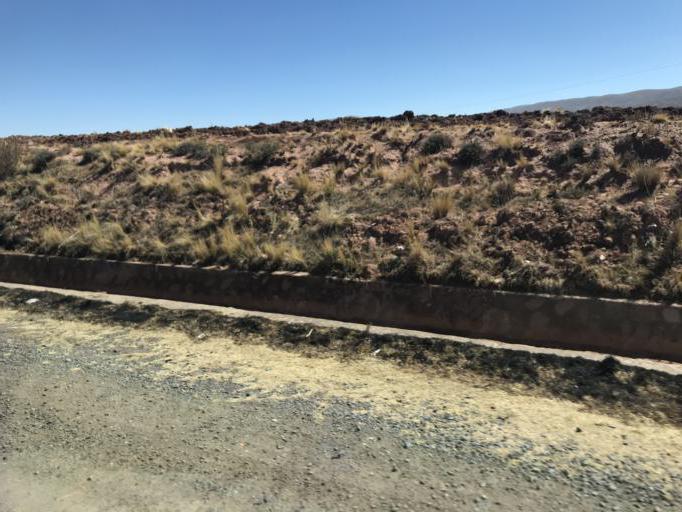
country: BO
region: La Paz
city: Tiahuanaco
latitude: -16.5946
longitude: -68.5756
